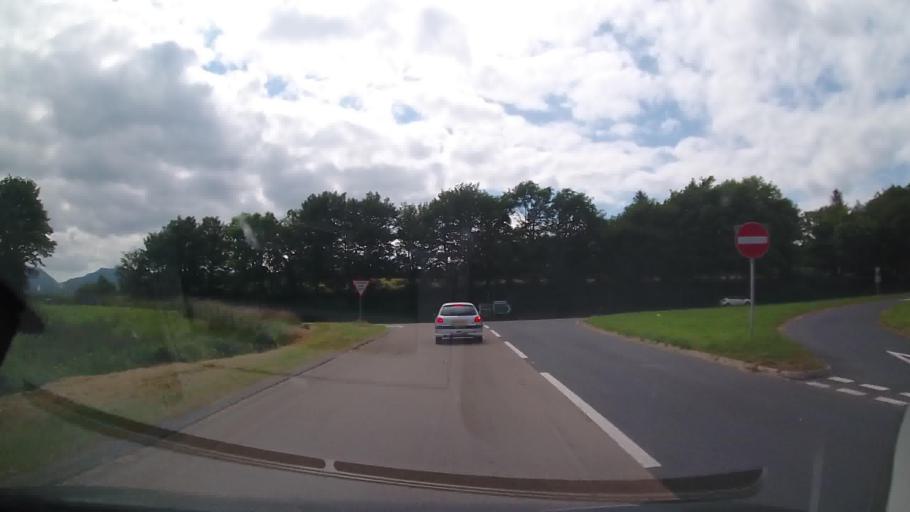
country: GB
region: Wales
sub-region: Gwynedd
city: Trawsfynydd
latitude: 52.9017
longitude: -3.9181
